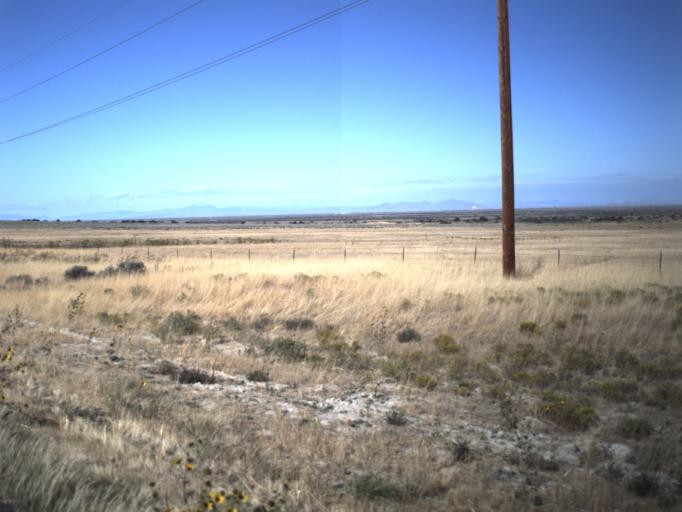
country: US
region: Utah
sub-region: Millard County
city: Delta
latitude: 39.4605
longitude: -112.2908
